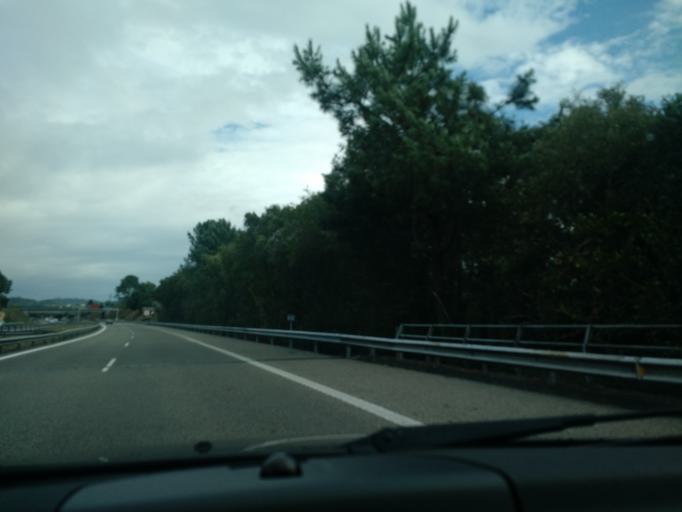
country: ES
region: Galicia
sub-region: Provincia da Coruna
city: Abegondo
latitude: 43.2539
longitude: -8.2540
